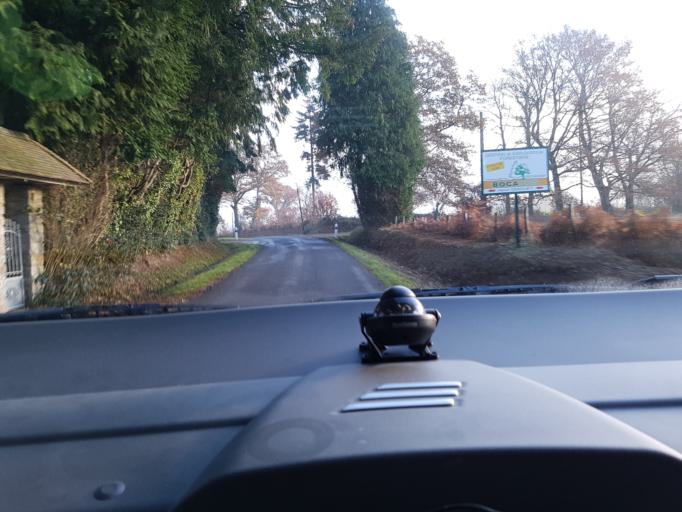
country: FR
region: Lower Normandy
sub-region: Departement de l'Orne
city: La Ferriere-aux-Etangs
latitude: 48.6337
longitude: -0.4897
